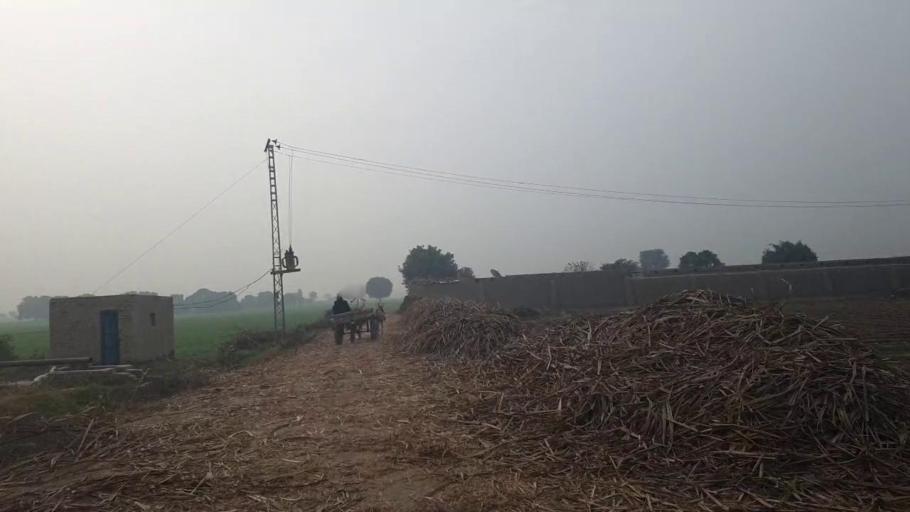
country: PK
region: Sindh
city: Tando Adam
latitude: 25.7086
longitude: 68.6522
